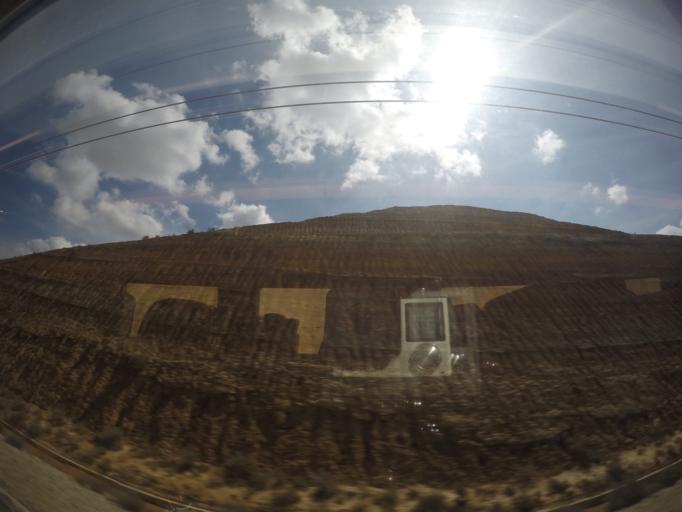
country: ES
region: Aragon
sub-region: Provincia de Huesca
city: Ballobar
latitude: 41.5785
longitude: 0.1231
